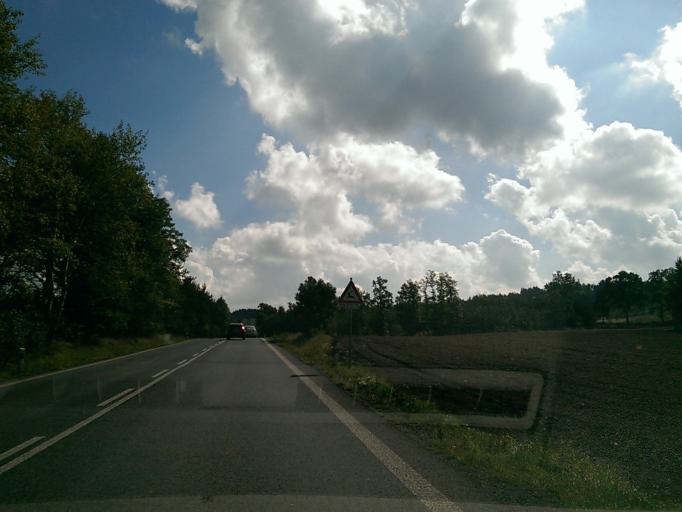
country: CZ
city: Doksy
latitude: 50.6029
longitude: 14.5905
